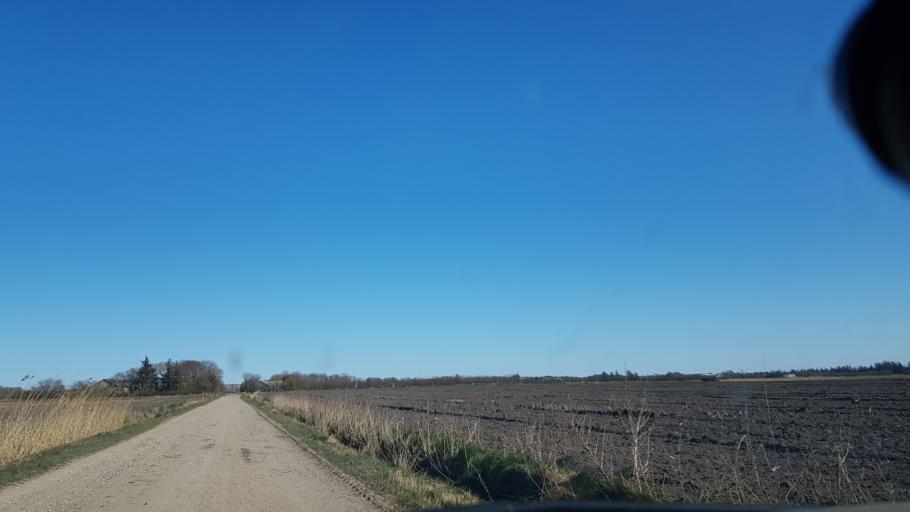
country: DK
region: South Denmark
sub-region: Tonder Kommune
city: Sherrebek
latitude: 55.2278
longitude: 8.7037
